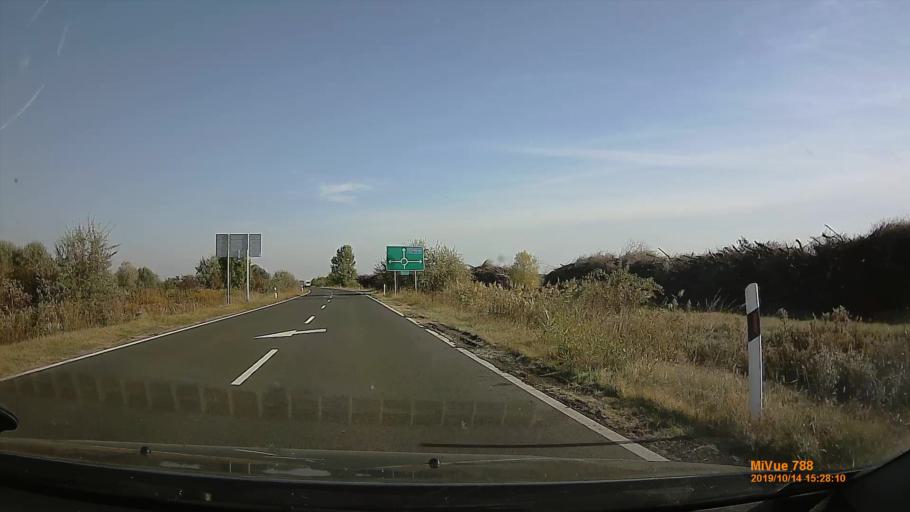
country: HU
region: Pest
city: Ecser
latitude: 47.4334
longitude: 19.3094
